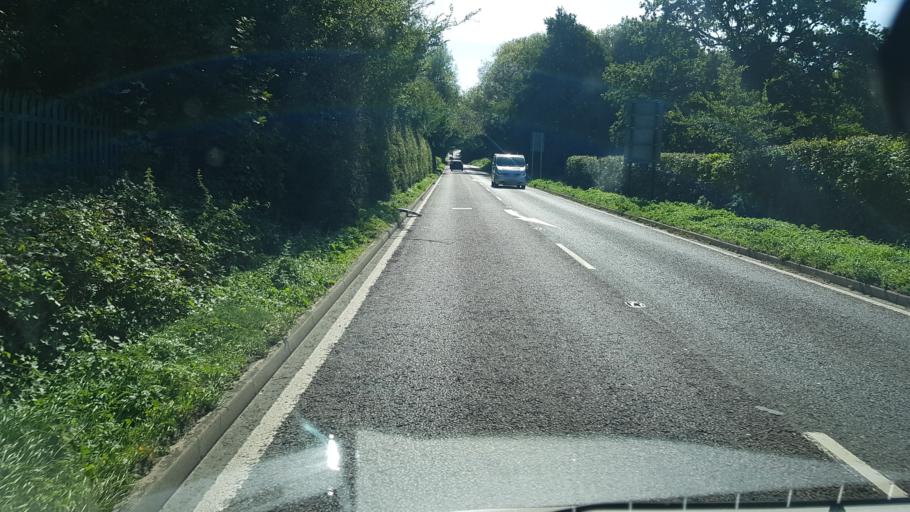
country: GB
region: England
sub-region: Kent
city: Kings Hill
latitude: 51.2553
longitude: 0.3702
